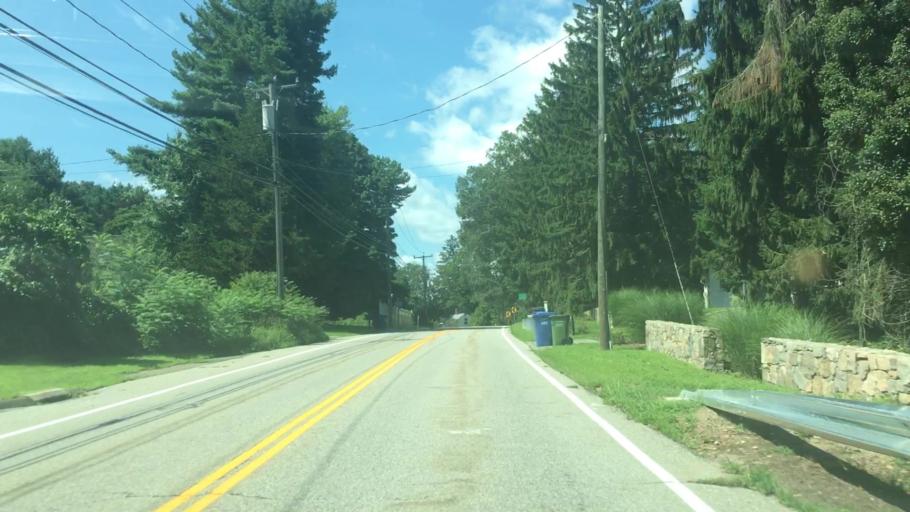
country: US
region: Connecticut
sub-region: Middlesex County
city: Essex Village
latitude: 41.3361
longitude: -72.3834
